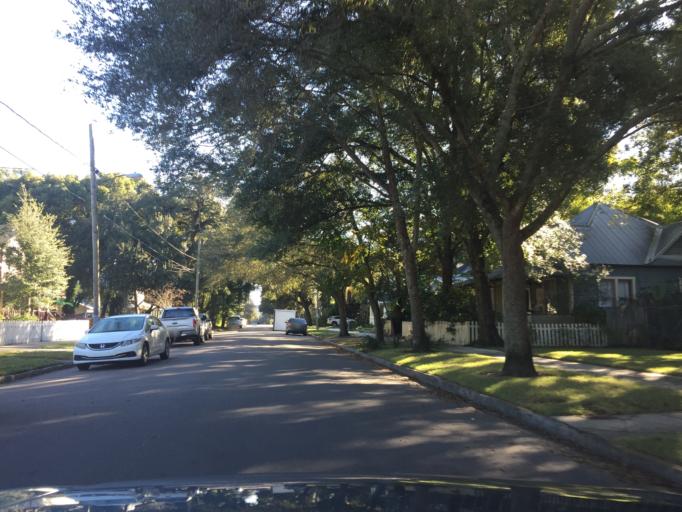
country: US
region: Florida
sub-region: Hillsborough County
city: Tampa
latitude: 27.9632
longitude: -82.4579
